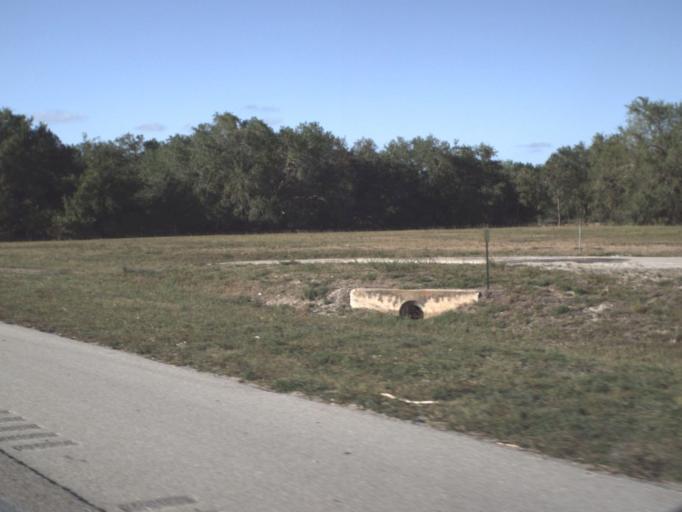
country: US
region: Florida
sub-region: Brevard County
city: South Patrick Shores
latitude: 28.2051
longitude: -80.7111
